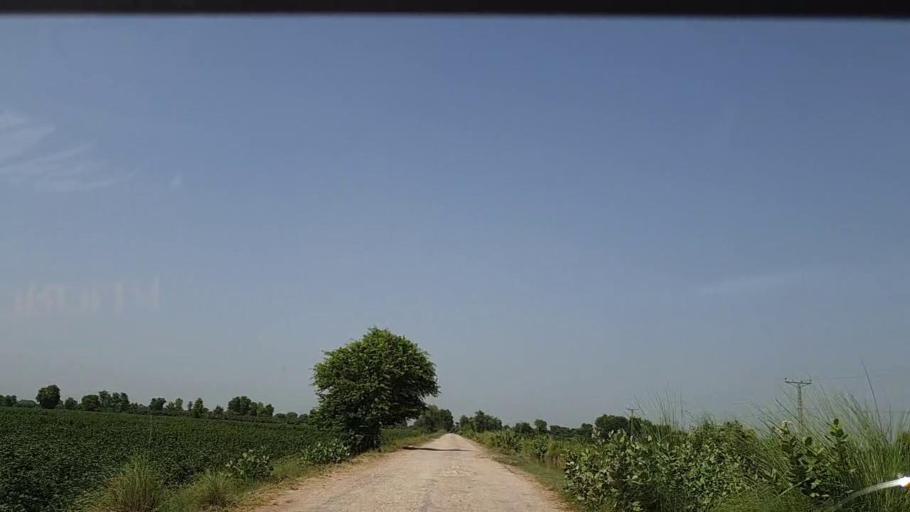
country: PK
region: Sindh
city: Kandiaro
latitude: 27.0360
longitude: 68.1567
